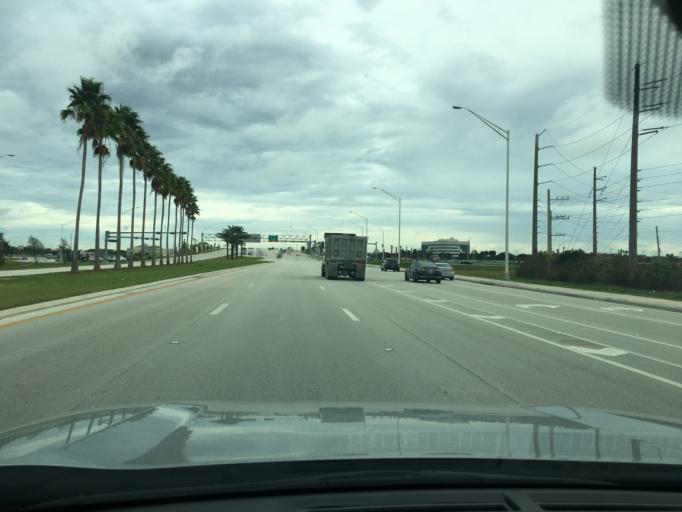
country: US
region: Florida
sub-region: Miami-Dade County
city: Palm Springs North
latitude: 25.9785
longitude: -80.3570
